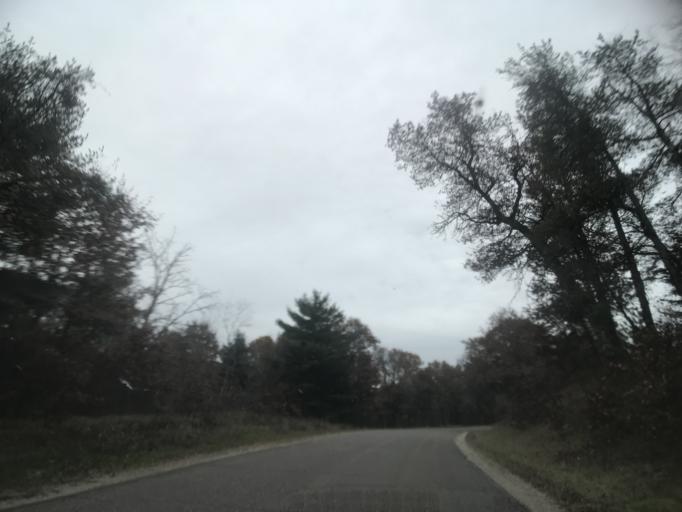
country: US
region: Wisconsin
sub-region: Oconto County
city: Gillett
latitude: 45.2631
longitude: -88.2528
